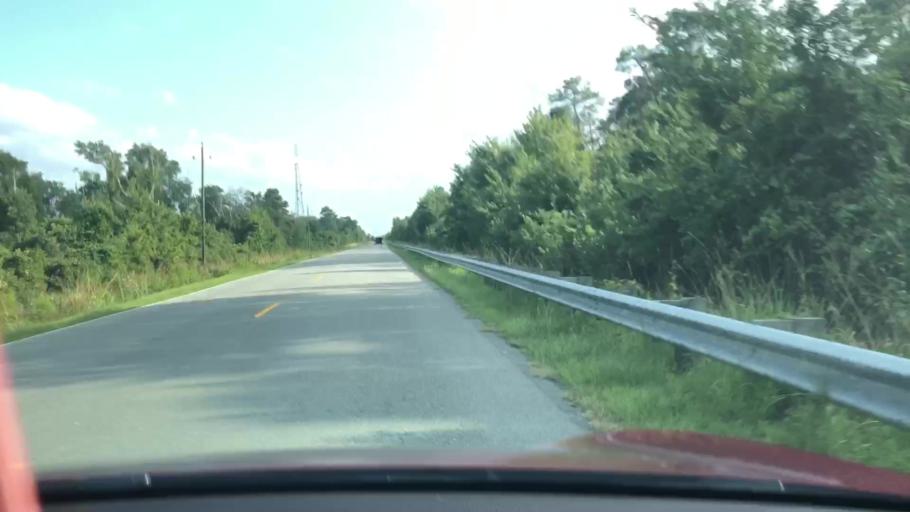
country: US
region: North Carolina
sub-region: Dare County
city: Wanchese
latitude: 35.7165
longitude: -75.7684
